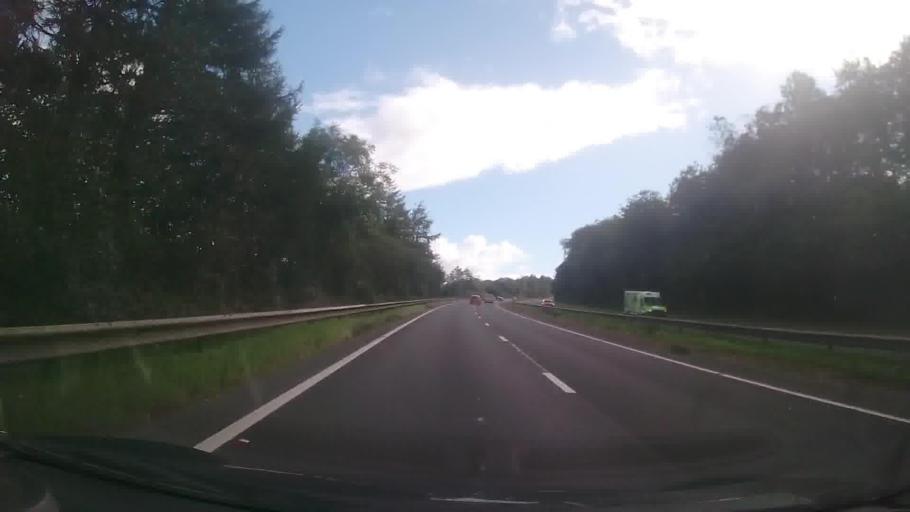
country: GB
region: Wales
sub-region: Carmarthenshire
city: Carmarthen
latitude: 51.8432
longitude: -4.2567
